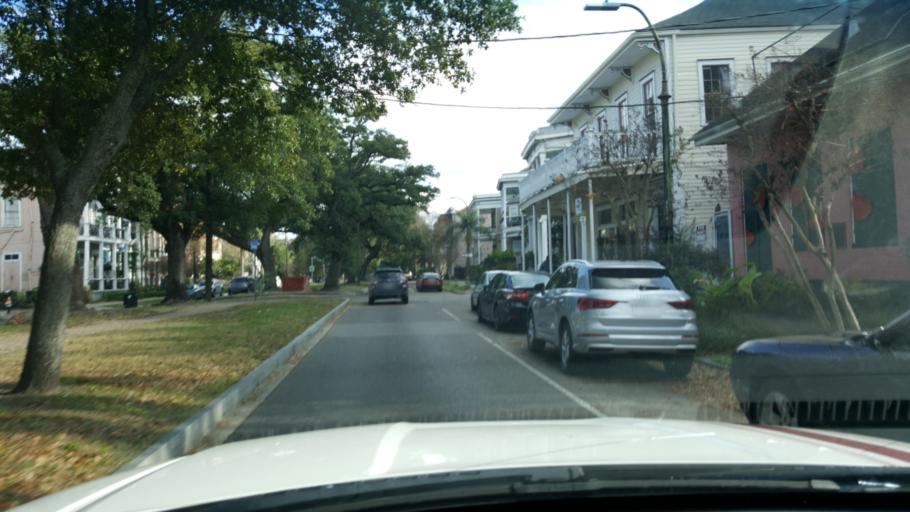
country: US
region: Louisiana
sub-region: Orleans Parish
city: New Orleans
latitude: 29.9678
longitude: -90.0664
